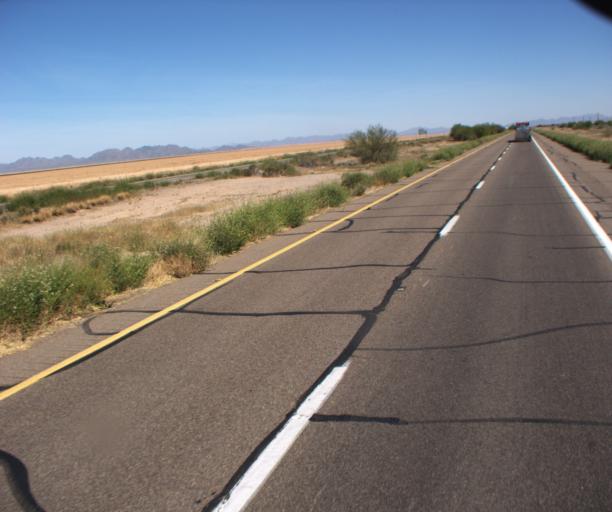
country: US
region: Arizona
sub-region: Maricopa County
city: Gila Bend
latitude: 32.9240
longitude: -112.8704
